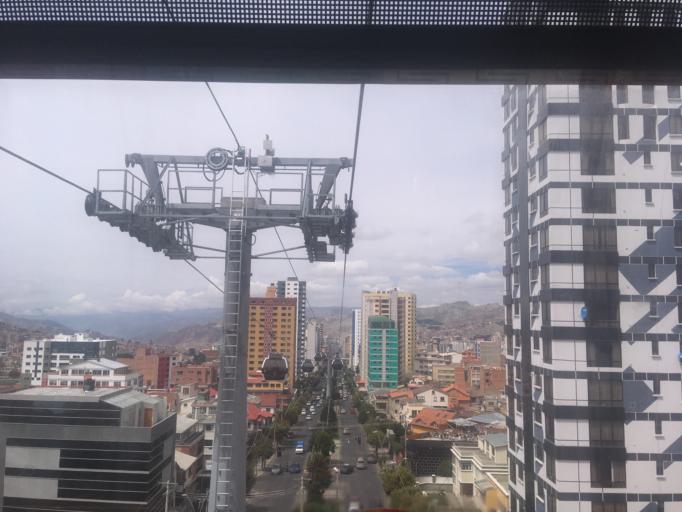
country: BO
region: La Paz
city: La Paz
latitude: -16.4863
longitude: -68.1218
